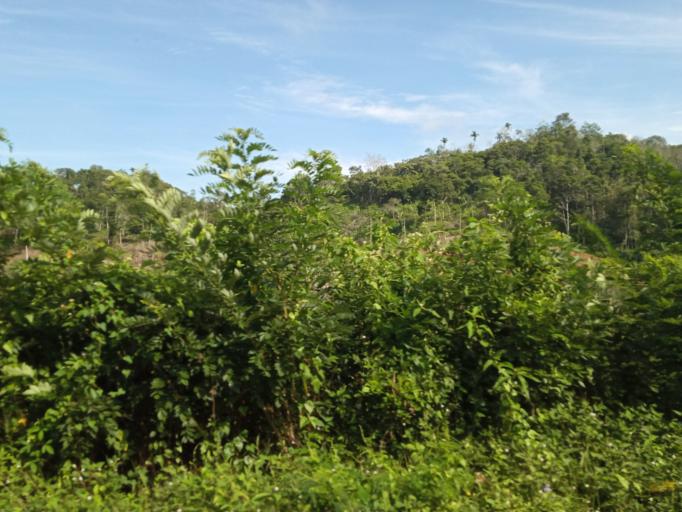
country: ID
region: Jambi
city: Sungai Penuh
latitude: -2.1494
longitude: 101.5670
